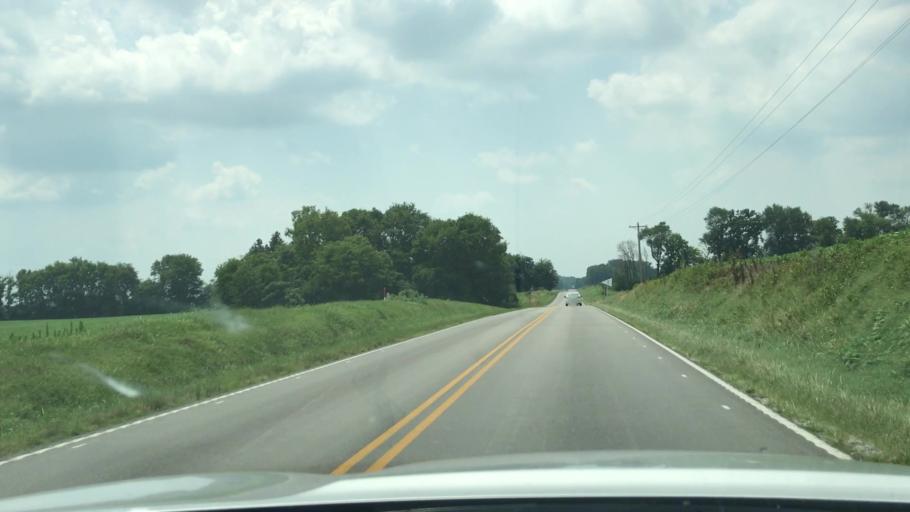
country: US
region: Kentucky
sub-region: Todd County
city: Guthrie
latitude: 36.7237
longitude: -87.0882
